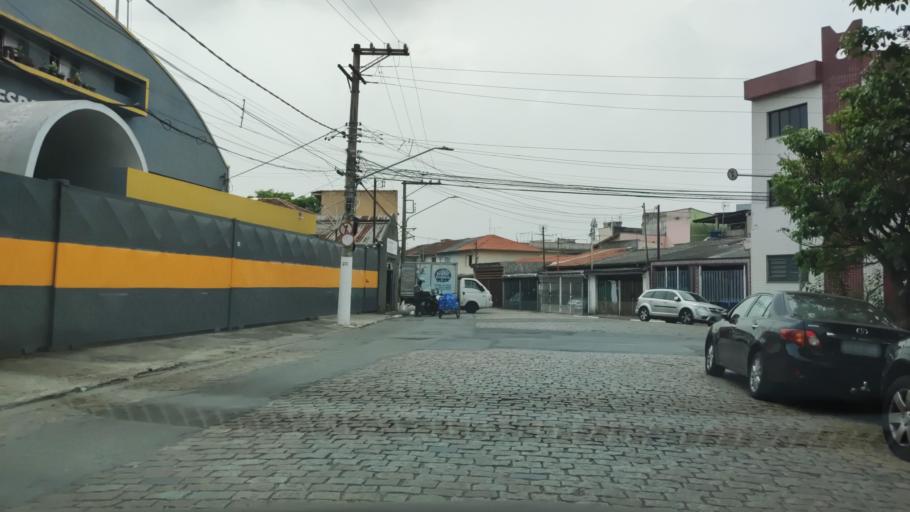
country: BR
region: Sao Paulo
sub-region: Sao Paulo
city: Sao Paulo
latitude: -23.5224
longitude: -46.6170
